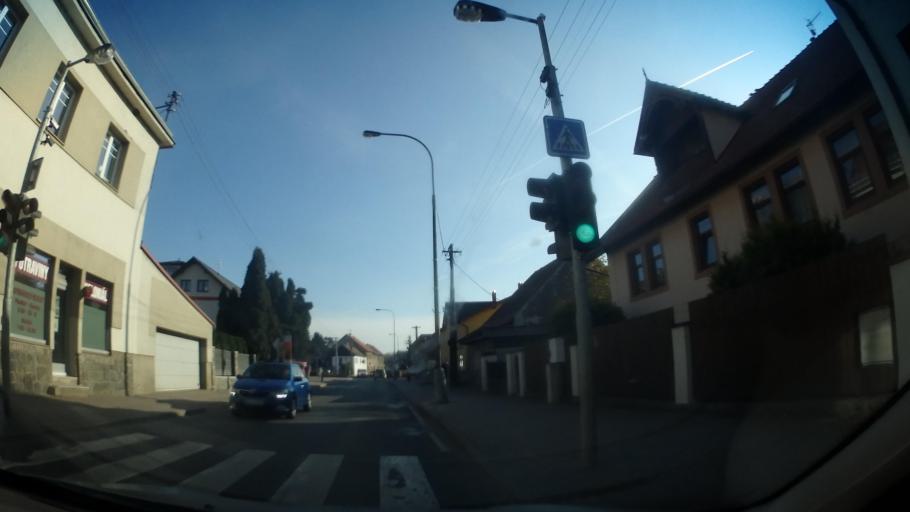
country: CZ
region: Central Bohemia
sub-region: Okres Praha-Vychod
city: Mnichovice
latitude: 49.9338
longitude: 14.7118
